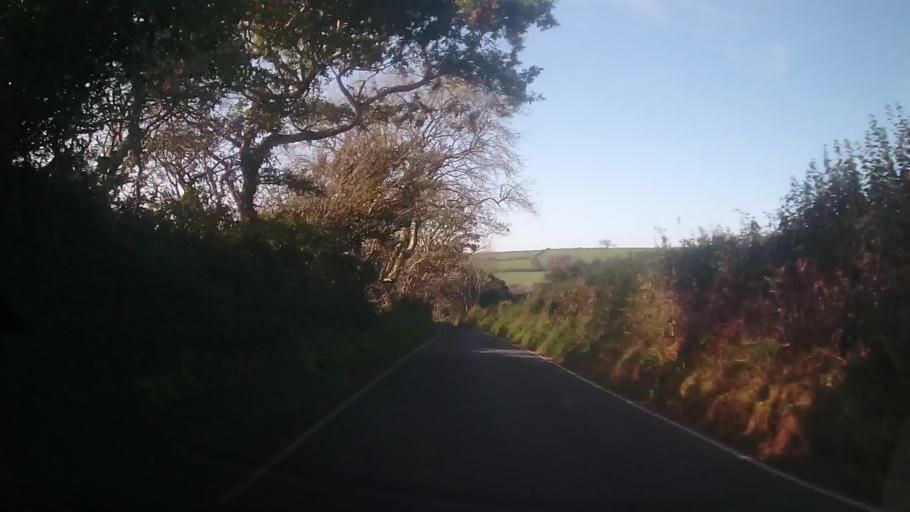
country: GB
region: Wales
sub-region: Pembrokeshire
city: Fishguard
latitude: 51.9750
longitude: -4.9153
